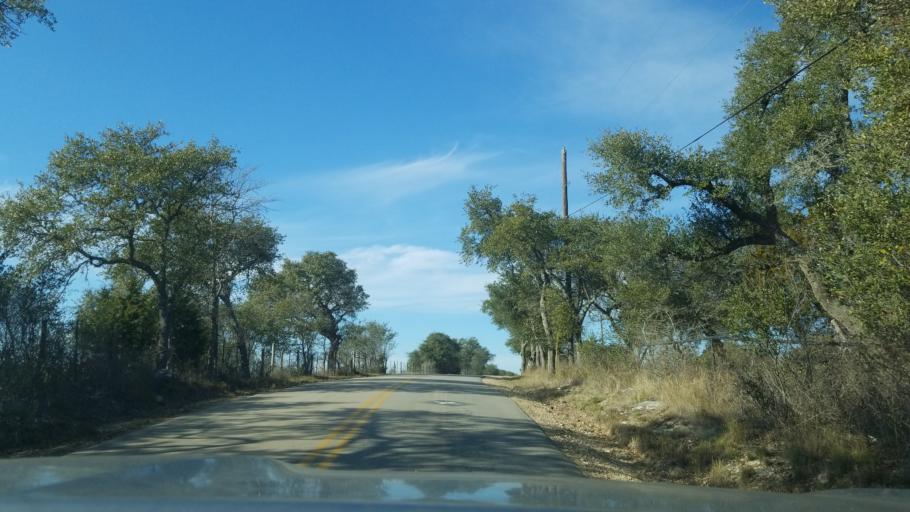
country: US
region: Texas
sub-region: Comal County
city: Canyon Lake
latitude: 29.7848
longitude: -98.2846
